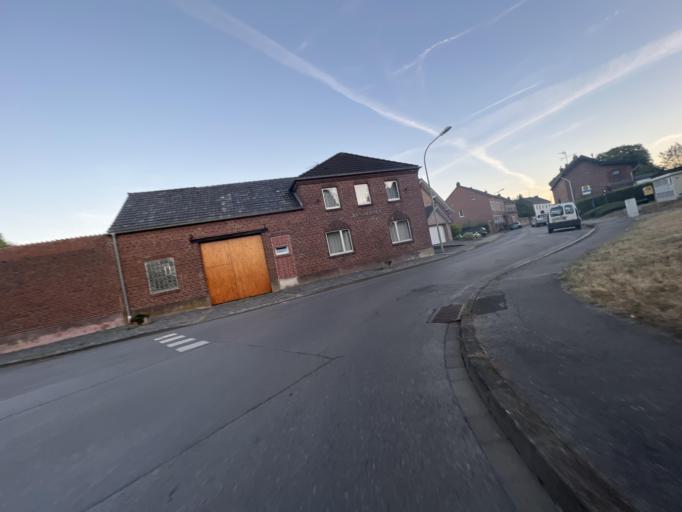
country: DE
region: North Rhine-Westphalia
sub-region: Regierungsbezirk Koln
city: Langerwehe
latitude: 50.8112
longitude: 6.4211
